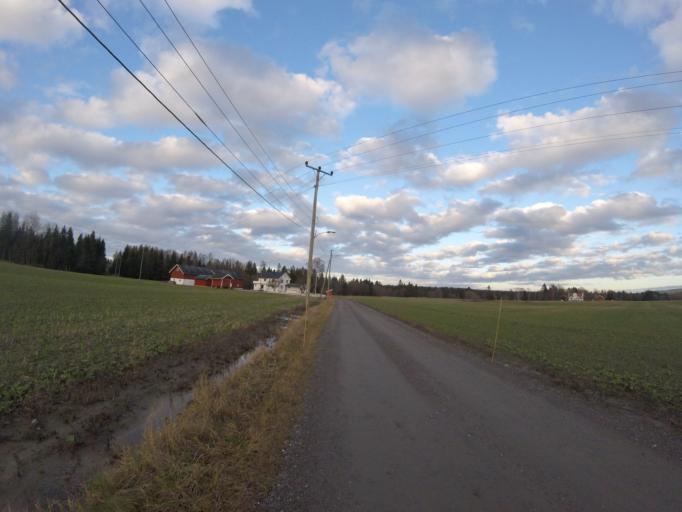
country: NO
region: Akershus
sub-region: Skedsmo
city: Leirsund
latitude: 59.9986
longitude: 11.0480
